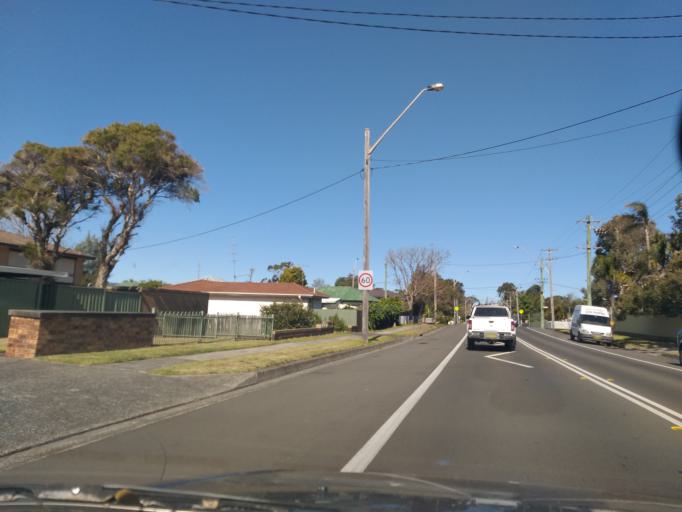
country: AU
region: New South Wales
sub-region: Wollongong
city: East Corrimal
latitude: -34.3631
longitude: 150.9114
